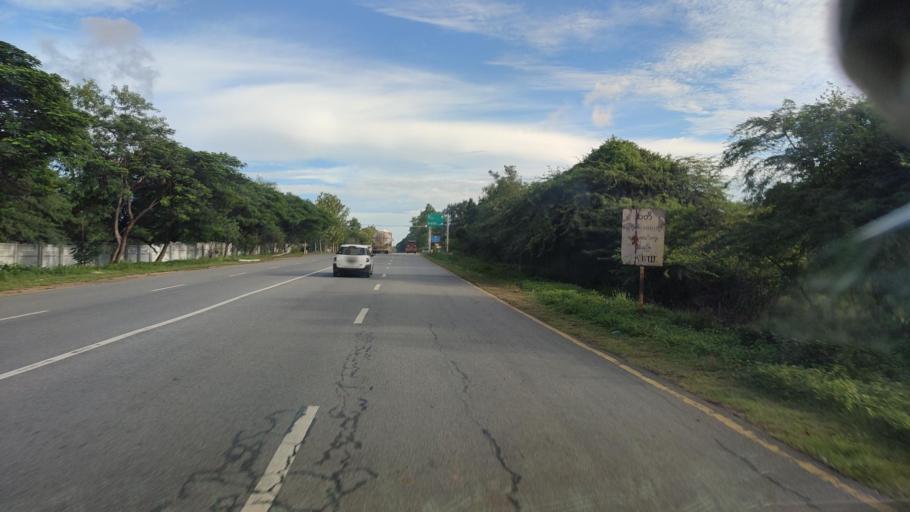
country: MM
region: Mandalay
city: Yamethin
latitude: 20.1606
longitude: 96.1907
